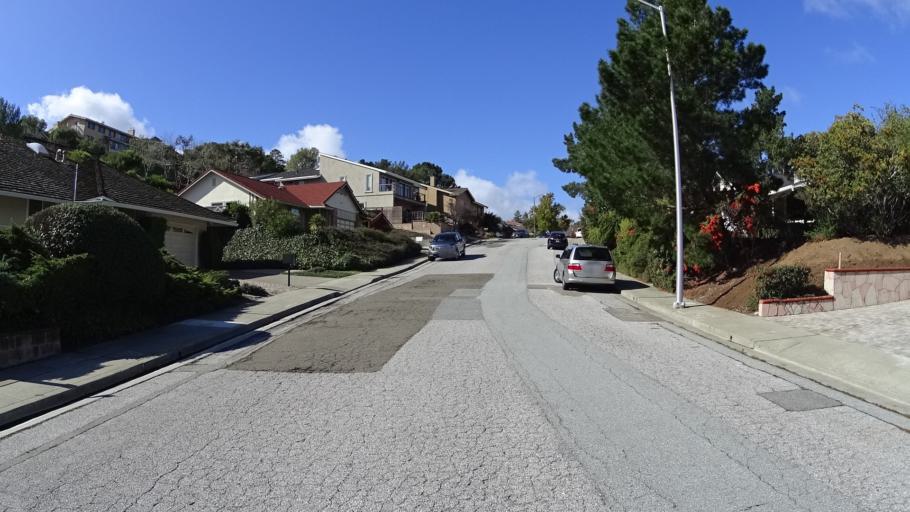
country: US
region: California
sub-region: San Mateo County
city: Millbrae
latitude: 37.5868
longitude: -122.4037
